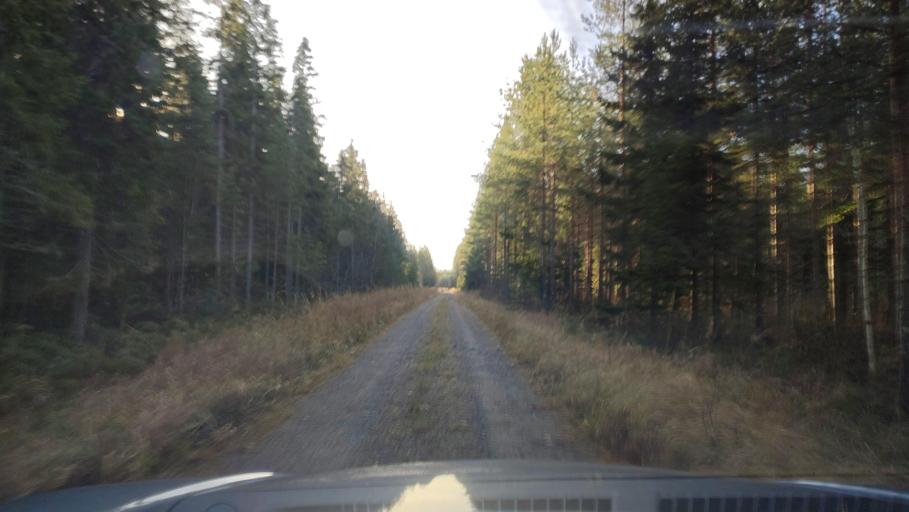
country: FI
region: Southern Ostrobothnia
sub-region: Suupohja
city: Karijoki
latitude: 62.1852
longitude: 21.6080
